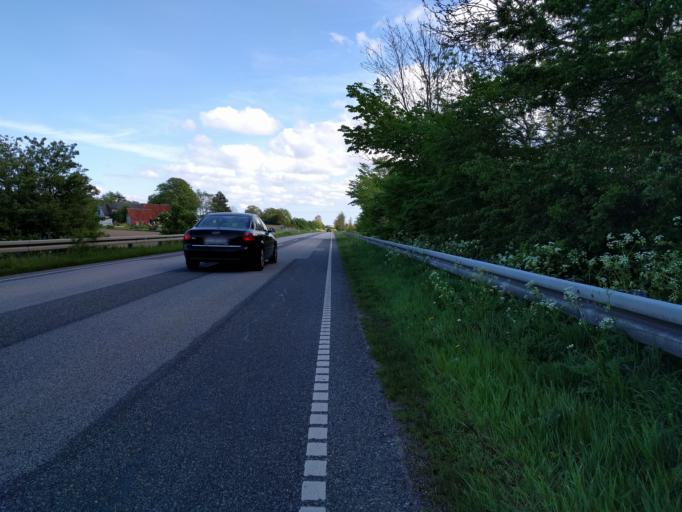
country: DK
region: Zealand
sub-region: Guldborgsund Kommune
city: Stubbekobing
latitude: 54.9277
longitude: 12.0174
